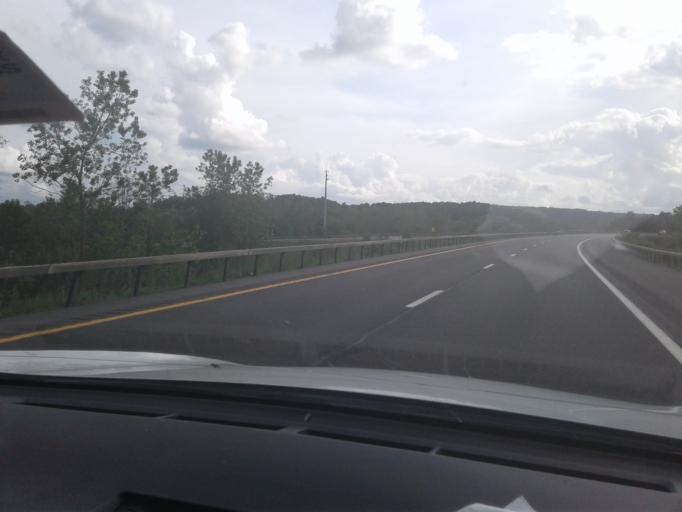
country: US
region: New York
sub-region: Onondaga County
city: East Syracuse
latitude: 43.0131
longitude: -76.0730
